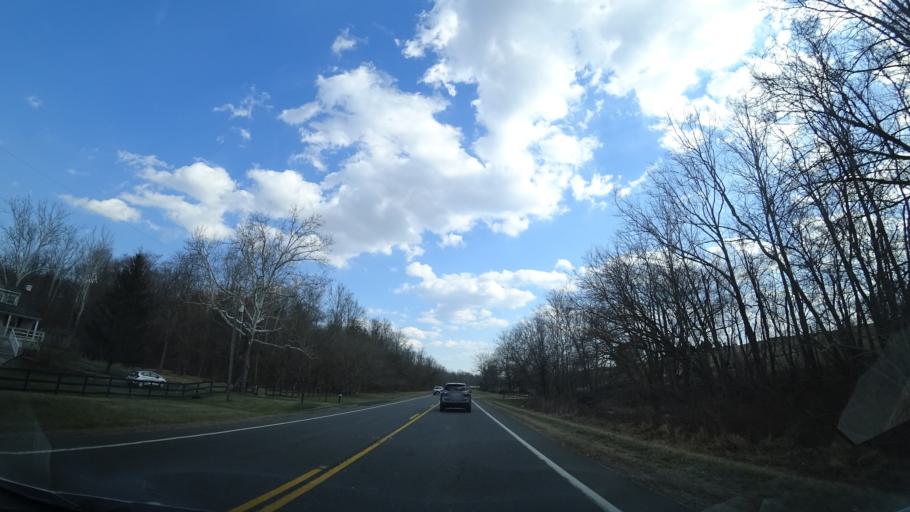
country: US
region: Virginia
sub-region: Fauquier County
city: Marshall
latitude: 38.9482
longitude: -77.9383
